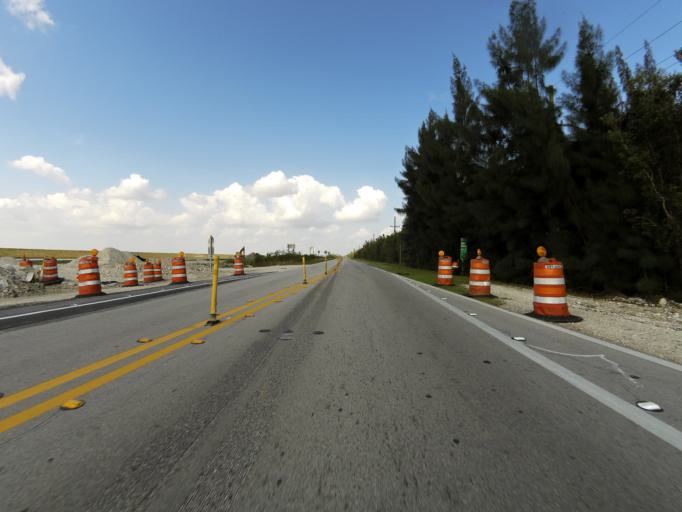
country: US
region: Florida
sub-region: Miami-Dade County
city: Palm Springs North
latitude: 25.9132
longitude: -80.4652
